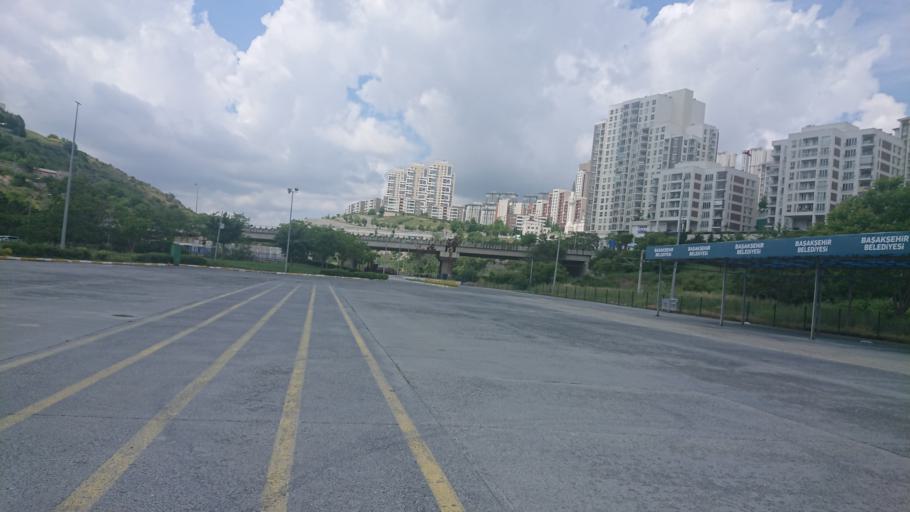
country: TR
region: Istanbul
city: Esenyurt
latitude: 41.0713
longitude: 28.6921
